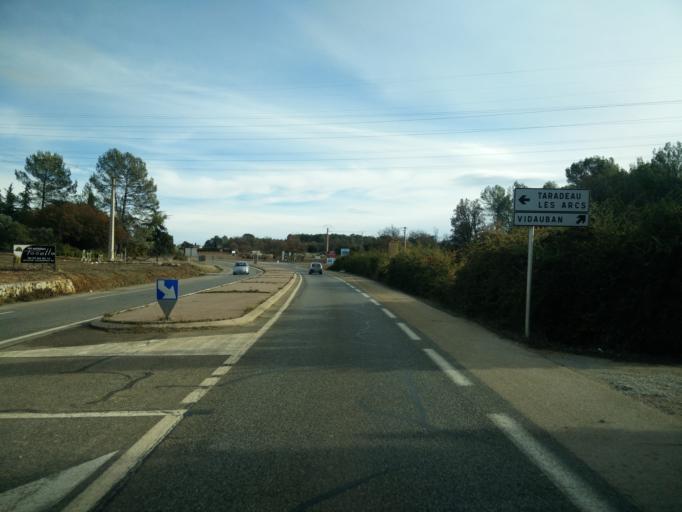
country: FR
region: Provence-Alpes-Cote d'Azur
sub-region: Departement du Var
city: Lorgues
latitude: 43.4674
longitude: 6.3865
